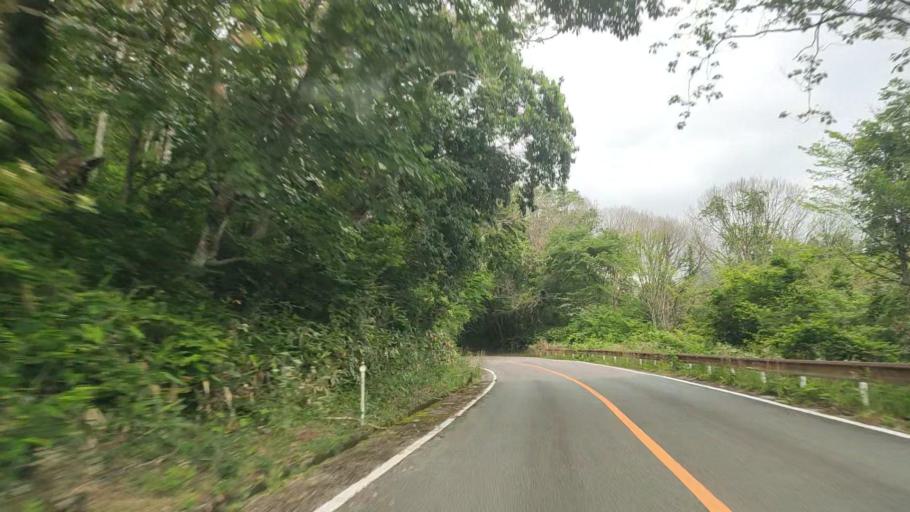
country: JP
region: Tottori
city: Kurayoshi
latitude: 35.3027
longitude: 133.6229
